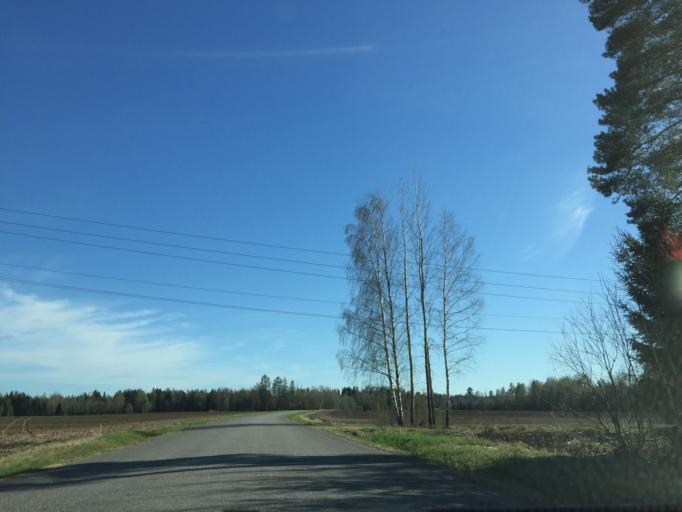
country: EE
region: Valgamaa
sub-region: Valga linn
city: Valga
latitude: 57.8557
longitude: 26.2535
